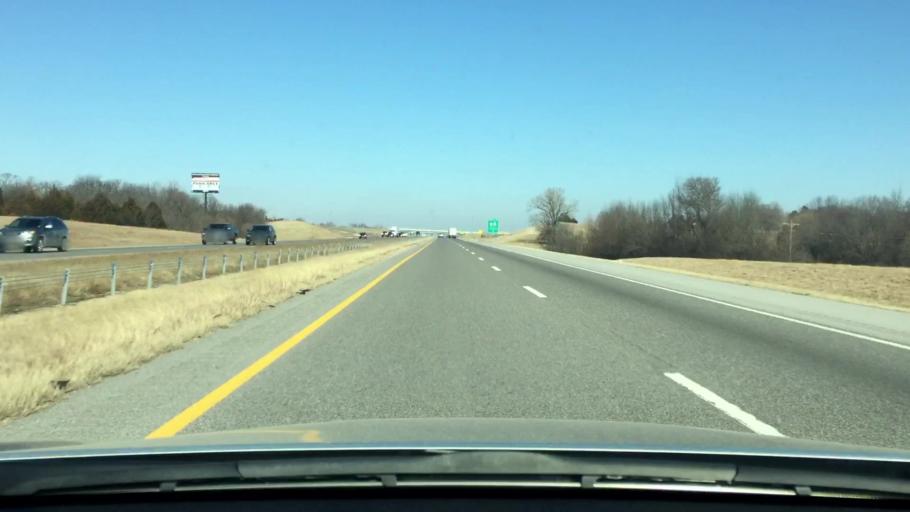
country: US
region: Oklahoma
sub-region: McClain County
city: Purcell
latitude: 34.9759
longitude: -97.3715
